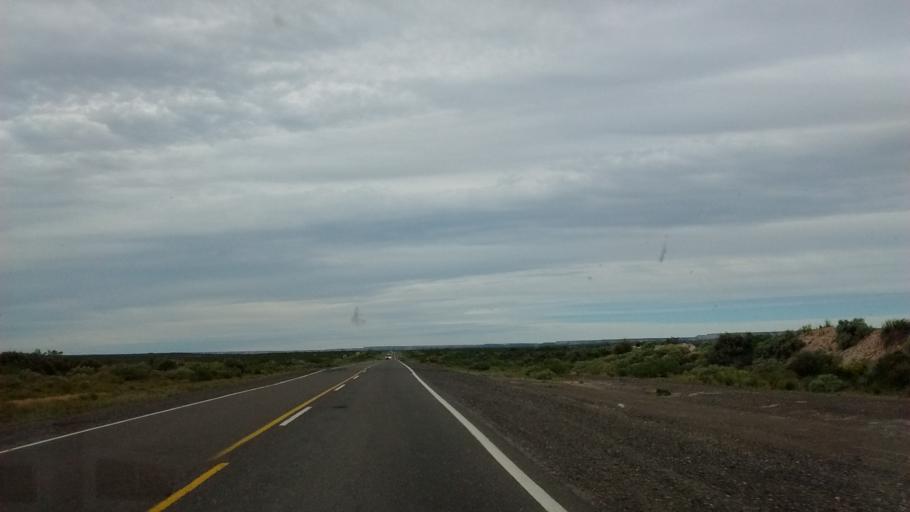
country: AR
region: Rio Negro
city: Catriel
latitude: -38.0901
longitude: -67.9263
